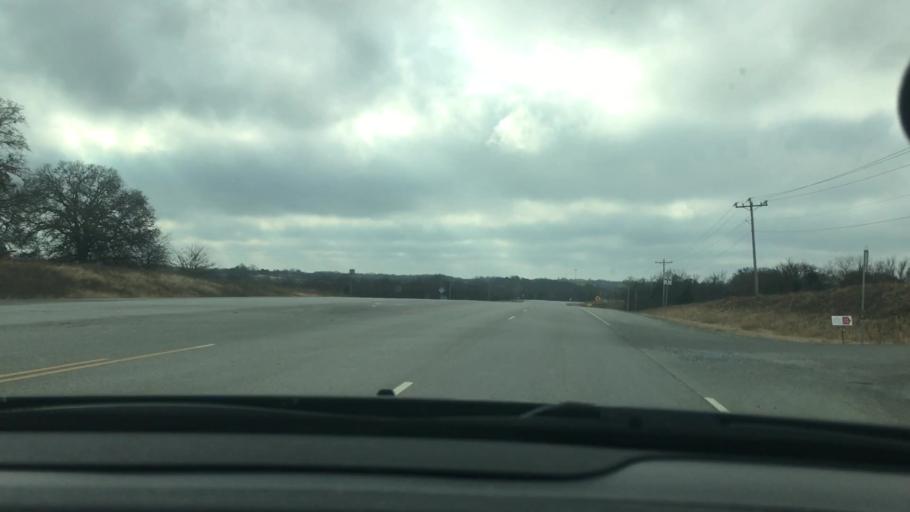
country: US
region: Oklahoma
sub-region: Bryan County
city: Durant
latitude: 34.0559
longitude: -96.3729
